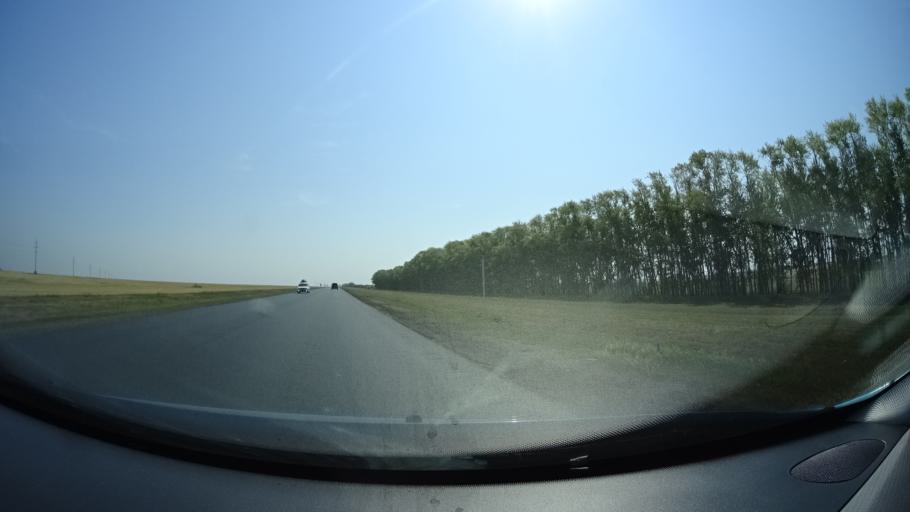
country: RU
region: Bashkortostan
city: Kabakovo
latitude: 54.4331
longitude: 56.0152
